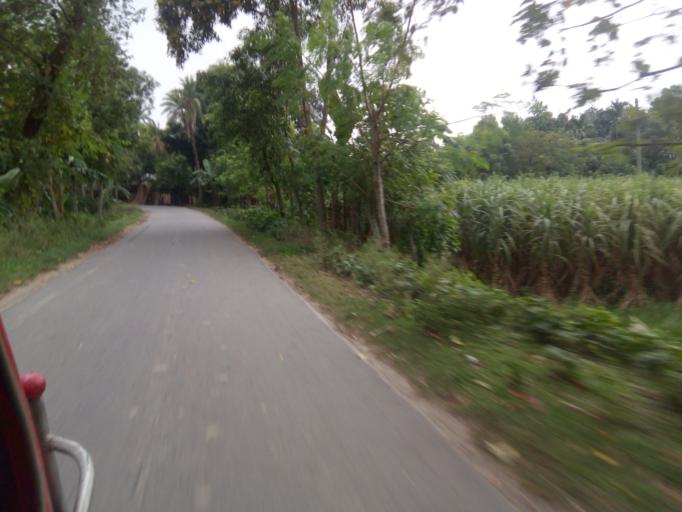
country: BD
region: Khulna
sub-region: Magura
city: Magura
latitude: 23.5245
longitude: 89.6148
